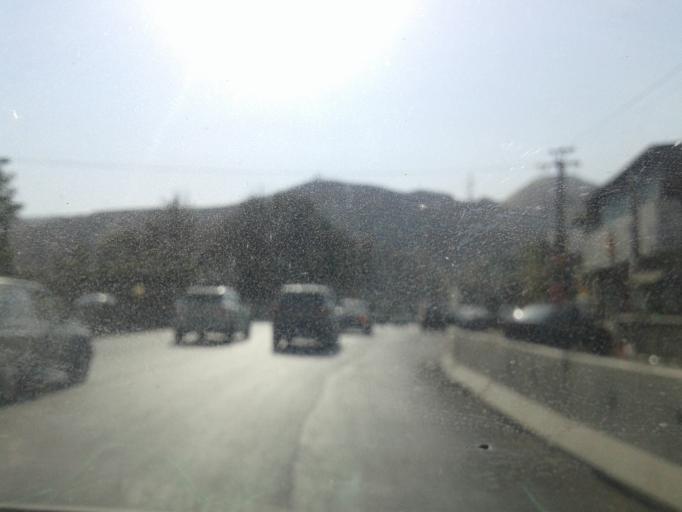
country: IR
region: Tehran
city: Pakdasht
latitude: 35.7418
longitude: 51.6980
